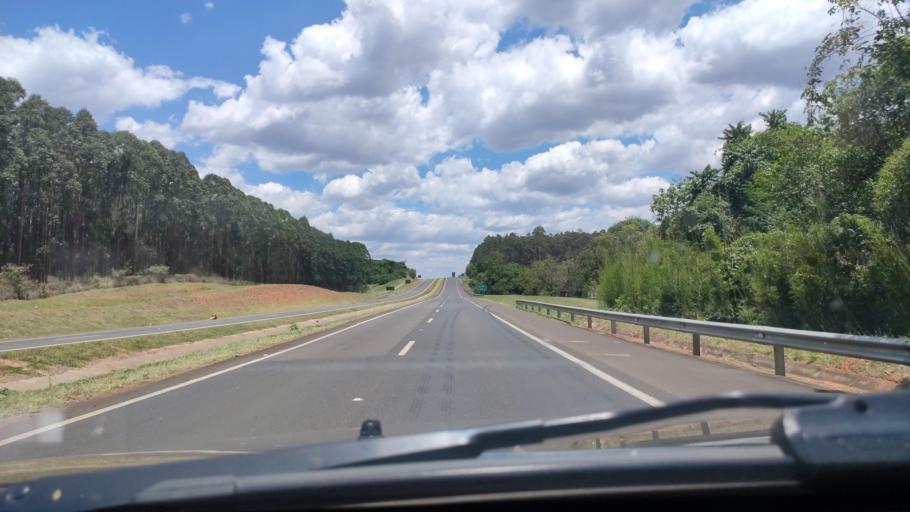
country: BR
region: Sao Paulo
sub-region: Duartina
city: Duartina
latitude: -22.4925
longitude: -49.2550
